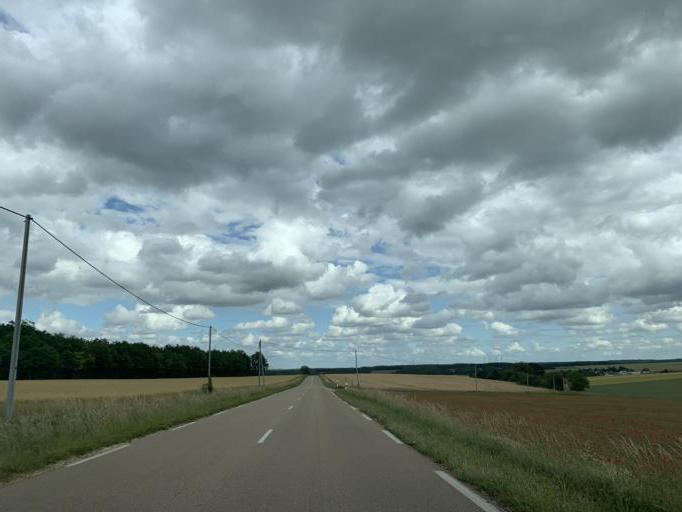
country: FR
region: Bourgogne
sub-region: Departement de l'Yonne
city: Chablis
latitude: 47.7375
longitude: 3.7718
